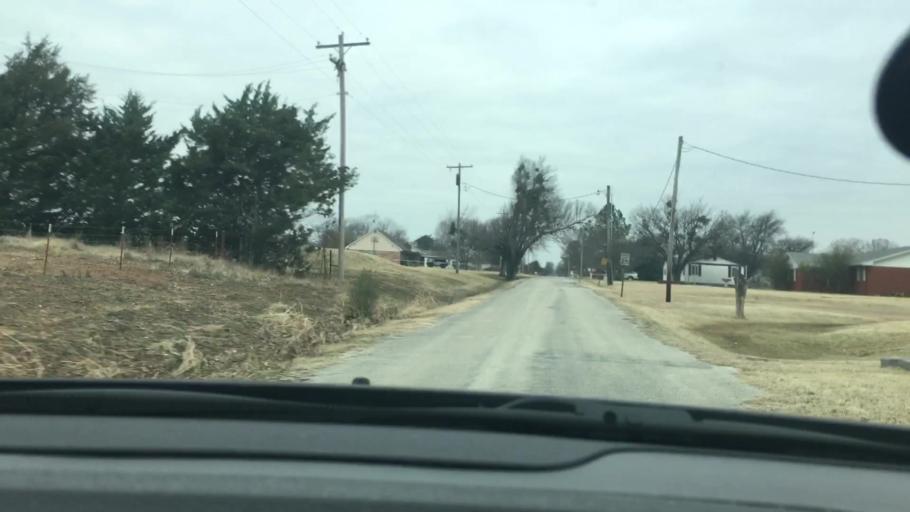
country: US
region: Oklahoma
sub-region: Carter County
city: Healdton
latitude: 34.2165
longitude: -97.4657
